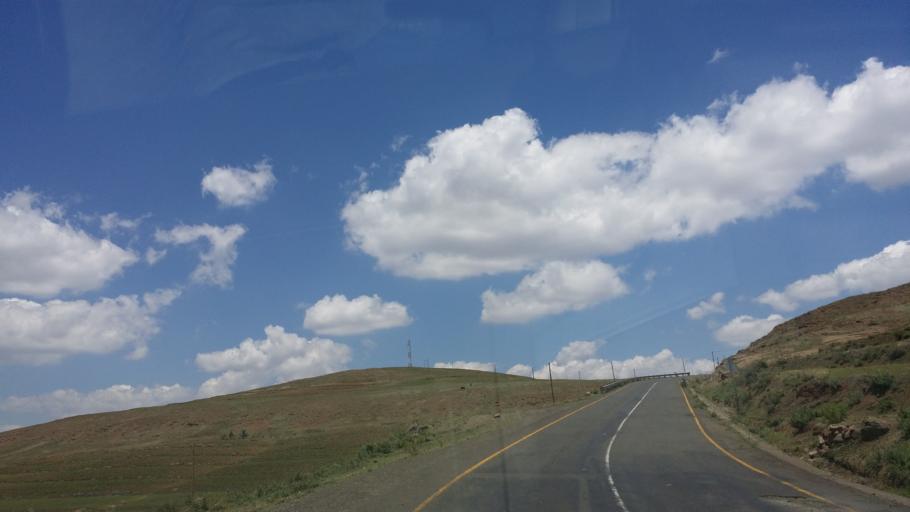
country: LS
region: Mokhotlong
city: Mokhotlong
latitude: -29.2638
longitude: 28.9045
